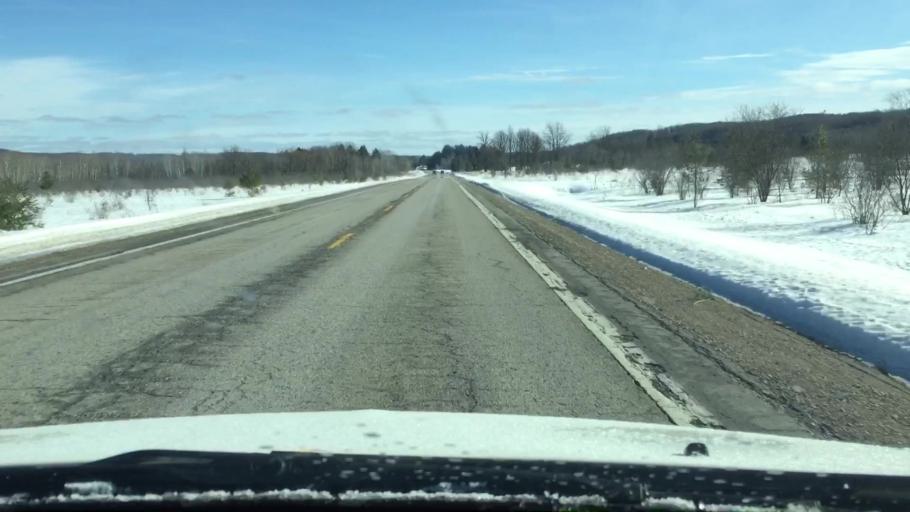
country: US
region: Michigan
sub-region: Charlevoix County
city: East Jordan
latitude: 45.1028
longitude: -85.1185
